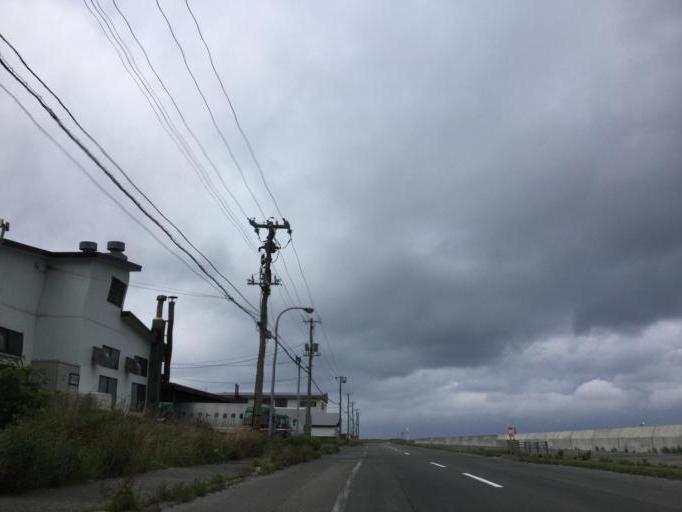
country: JP
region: Hokkaido
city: Wakkanai
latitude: 45.3987
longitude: 141.7063
